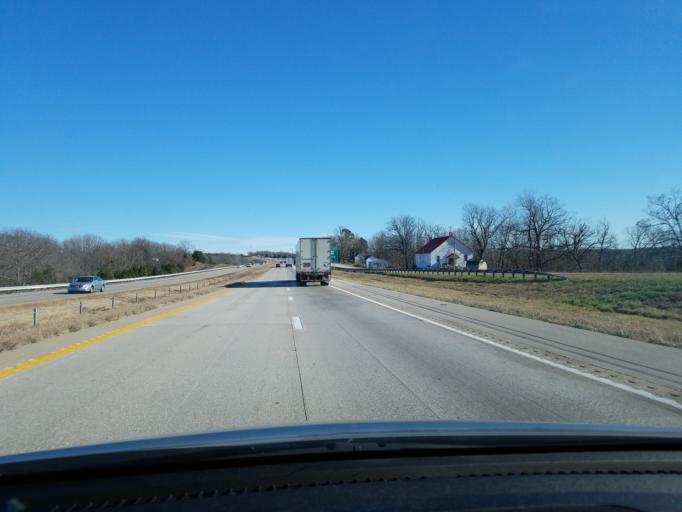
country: US
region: Missouri
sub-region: Pulaski County
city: Richland
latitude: 37.7685
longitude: -92.4314
